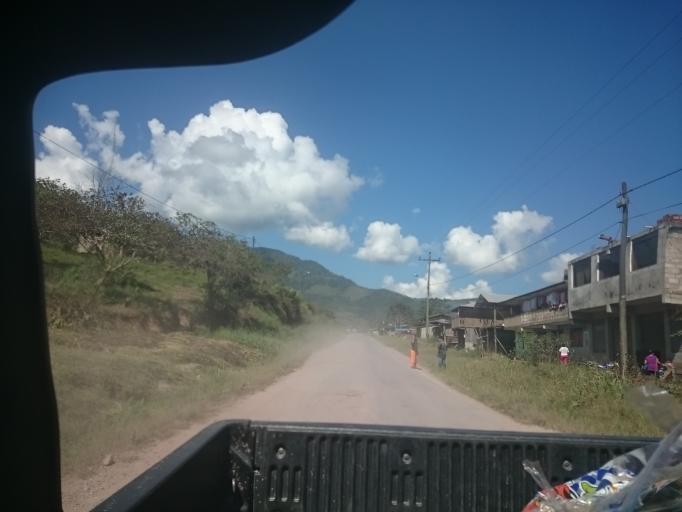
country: PE
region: Pasco
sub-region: Provincia de Oxapampa
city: Villa Rica
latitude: -10.6636
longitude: -75.1189
